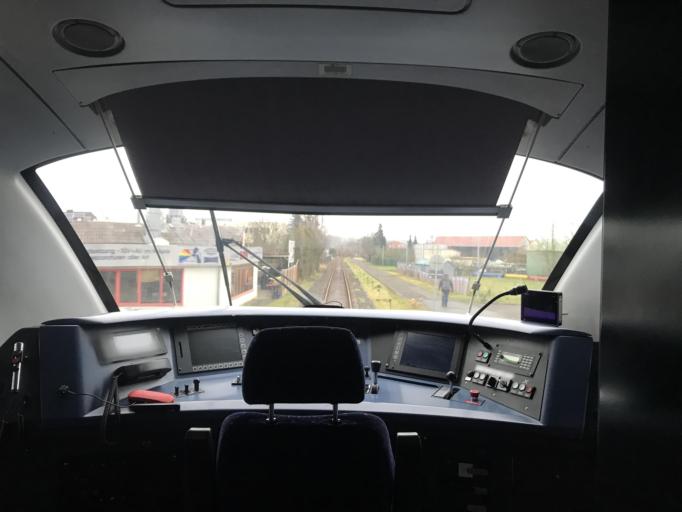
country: DE
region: Hesse
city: Fritzlar
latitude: 51.1238
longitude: 9.2752
